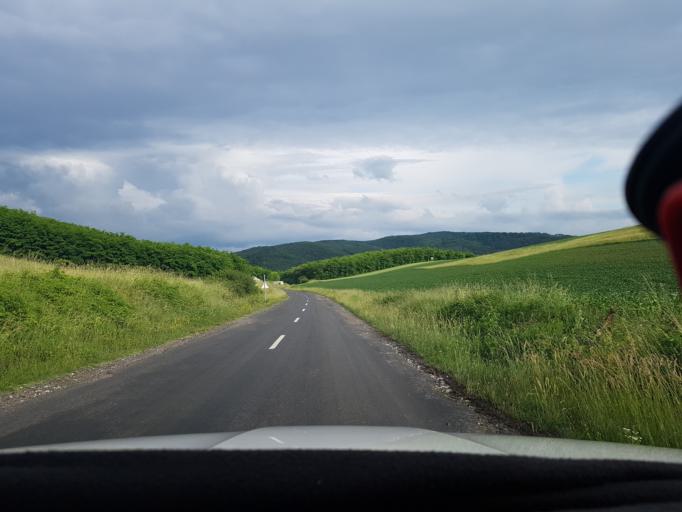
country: HU
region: Komarom-Esztergom
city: Nyergesujfalu
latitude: 47.7206
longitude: 18.5513
